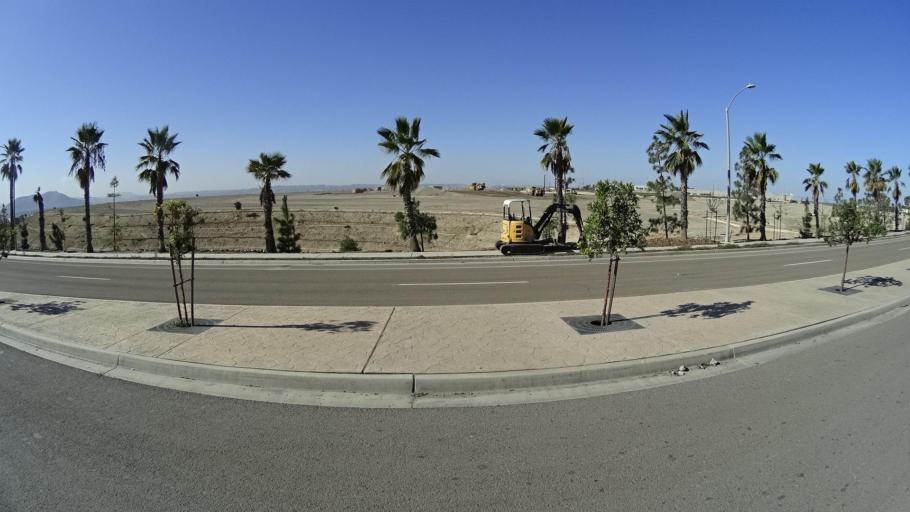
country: MX
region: Baja California
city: Tijuana
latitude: 32.5700
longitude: -116.9140
